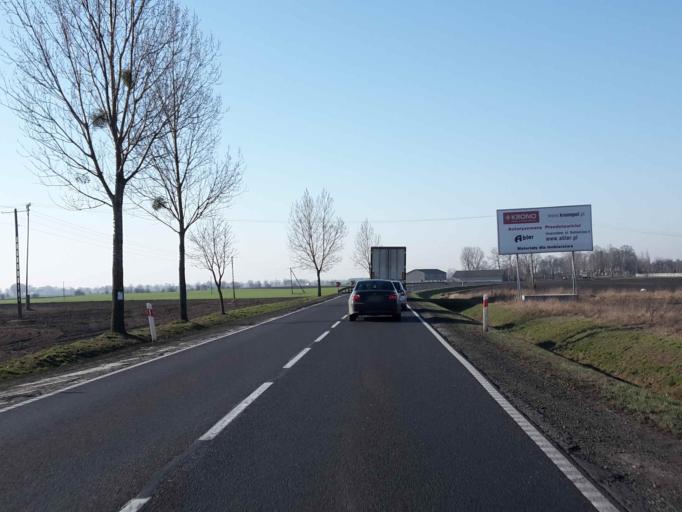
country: PL
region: Kujawsko-Pomorskie
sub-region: Powiat inowroclawski
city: Wierzchoslawice
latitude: 52.8548
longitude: 18.3488
